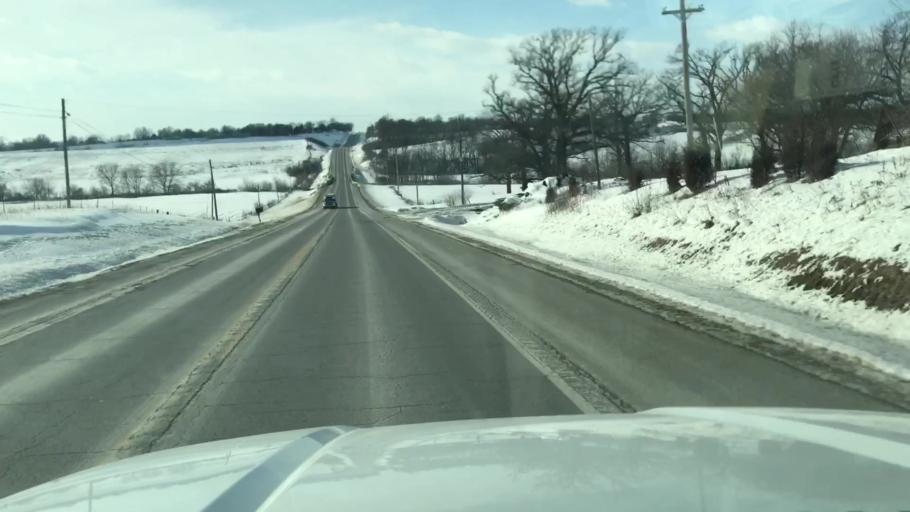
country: US
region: Missouri
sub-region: Nodaway County
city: Maryville
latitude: 40.3446
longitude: -94.7756
